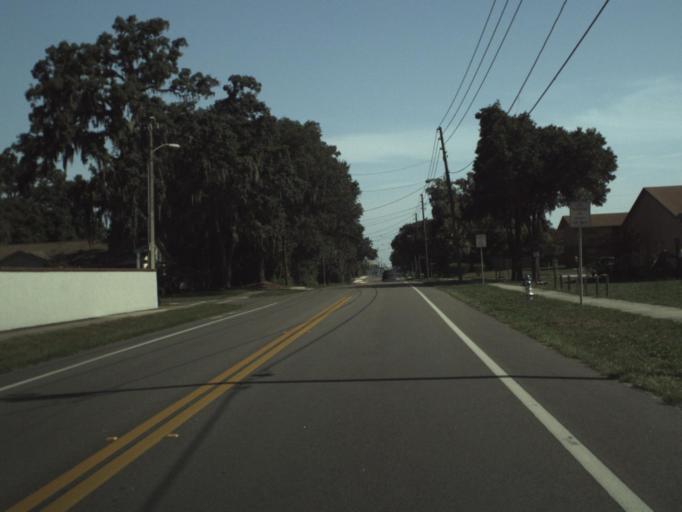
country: US
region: Florida
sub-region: Seminole County
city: Oviedo
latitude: 28.6625
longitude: -81.2084
